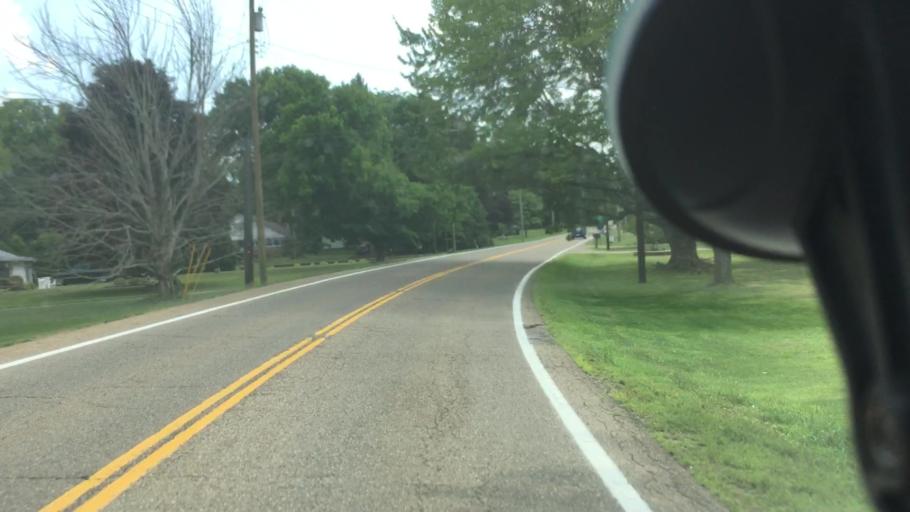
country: US
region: Ohio
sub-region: Columbiana County
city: Salem
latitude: 40.9184
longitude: -80.8405
